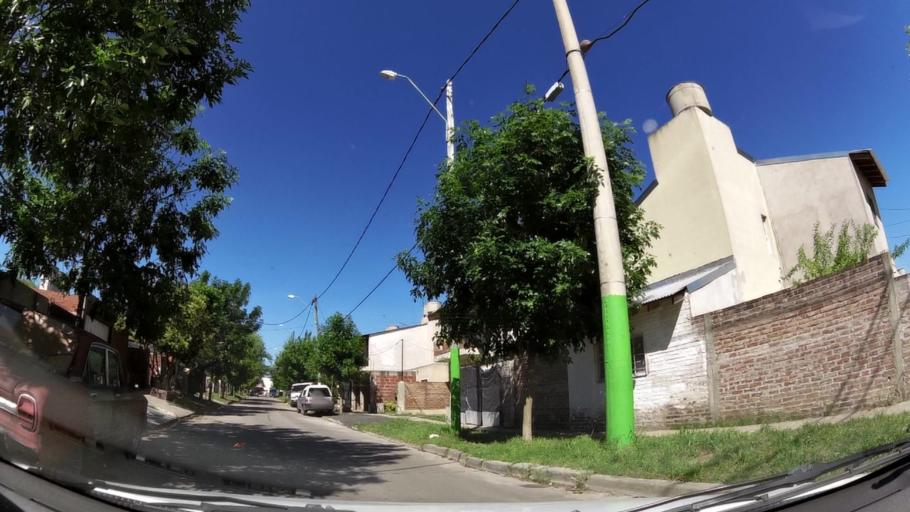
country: AR
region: Buenos Aires
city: Hurlingham
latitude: -34.6193
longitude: -58.6509
